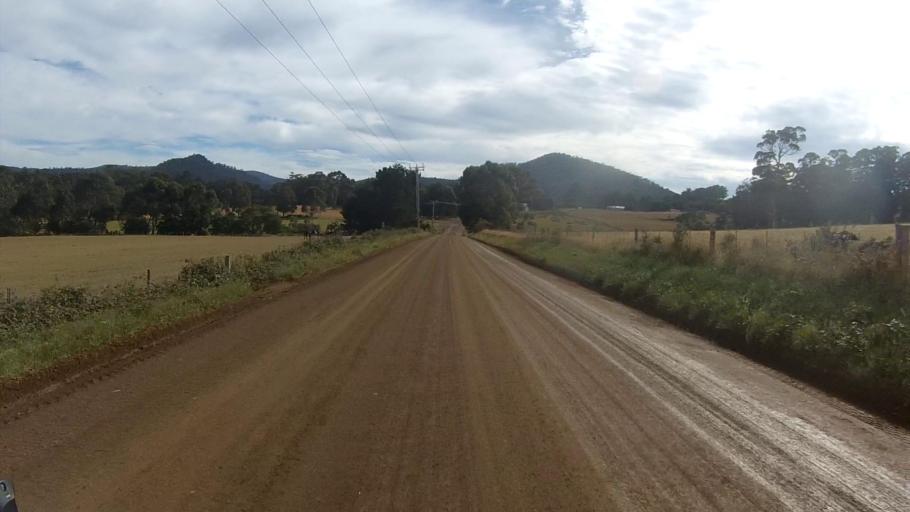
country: AU
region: Tasmania
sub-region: Sorell
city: Sorell
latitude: -42.7824
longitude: 147.8089
